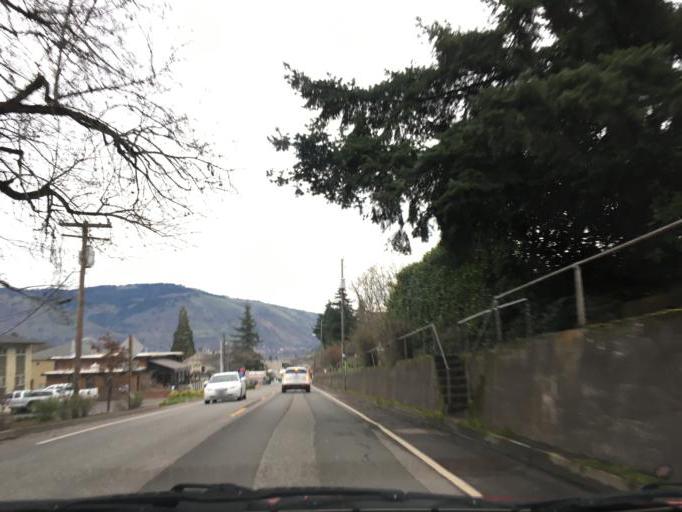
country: US
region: Oregon
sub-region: Hood River County
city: Hood River
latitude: 45.7087
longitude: -121.5188
